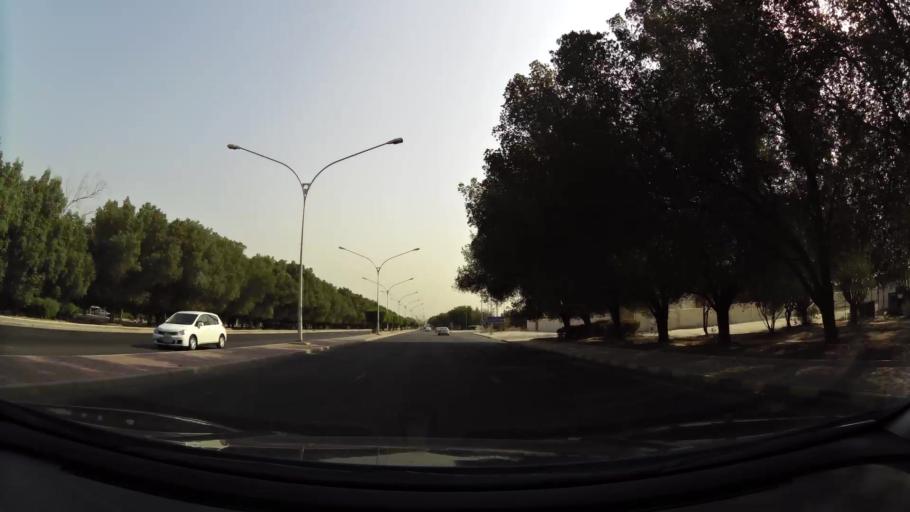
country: KW
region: Mubarak al Kabir
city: Sabah as Salim
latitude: 29.2747
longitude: 48.0640
